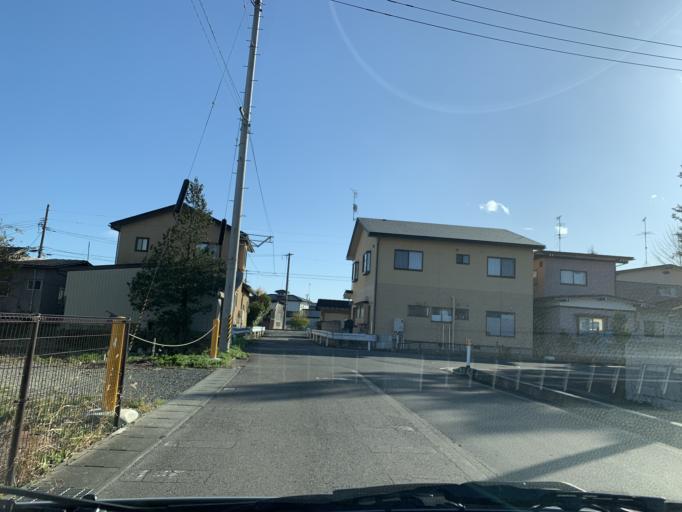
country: JP
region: Iwate
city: Kitakami
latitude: 39.2324
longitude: 141.0838
